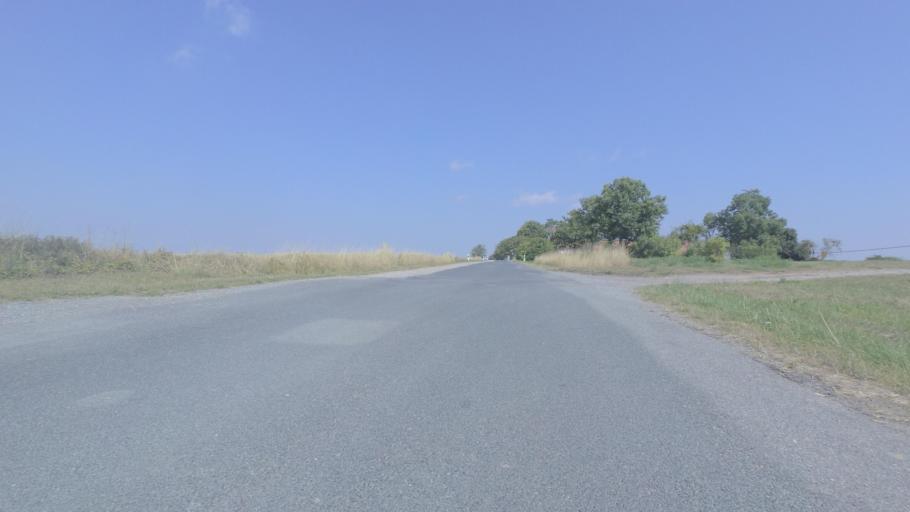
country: DE
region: Mecklenburg-Vorpommern
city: Pampow
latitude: 53.6910
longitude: 12.5990
